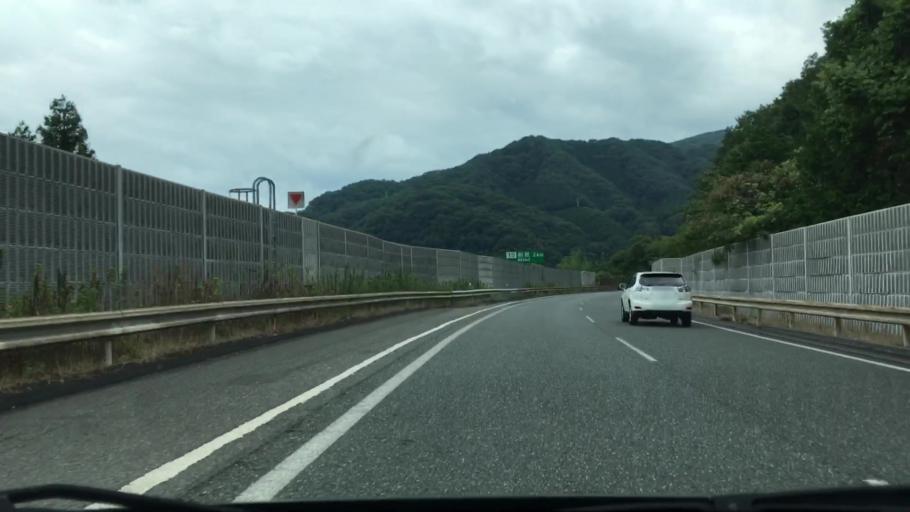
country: JP
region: Okayama
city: Niimi
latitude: 34.9932
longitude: 133.4673
